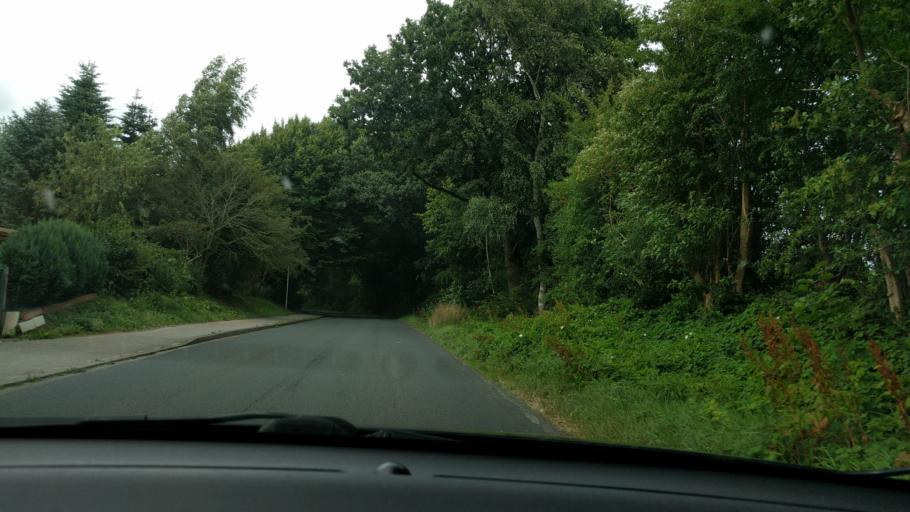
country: DE
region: Schleswig-Holstein
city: Wesseln
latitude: 54.2054
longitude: 9.0928
